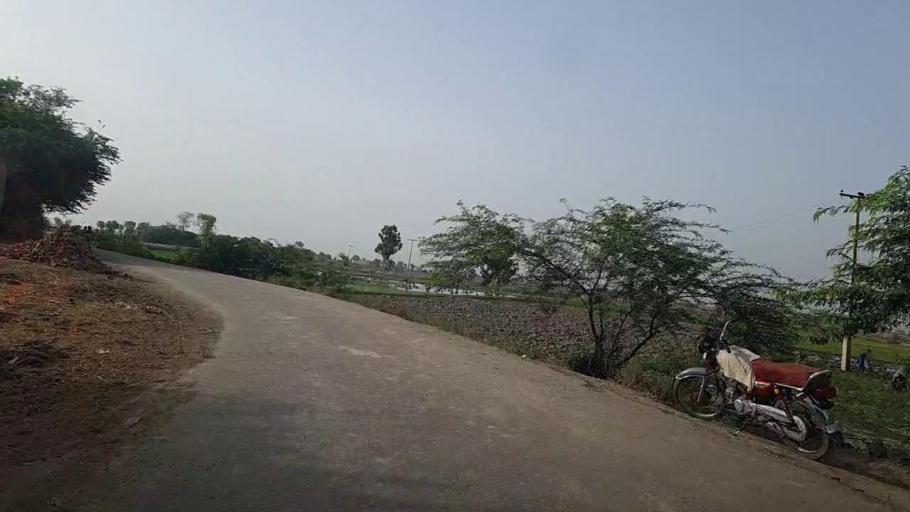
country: PK
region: Sindh
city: Khairpur Nathan Shah
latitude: 27.1086
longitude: 67.7914
